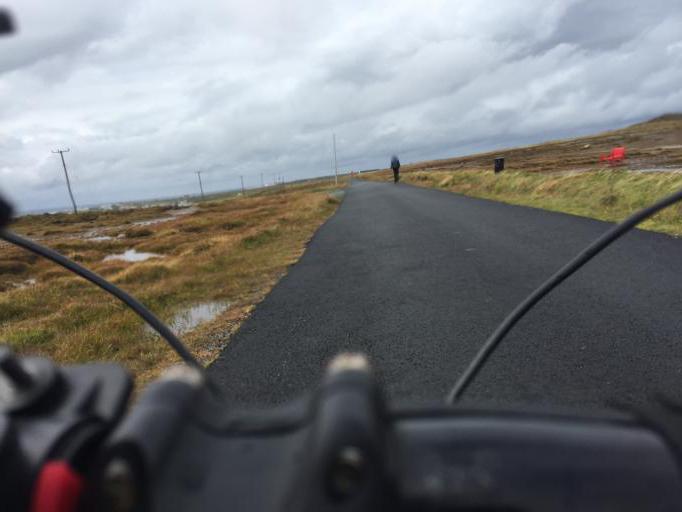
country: IE
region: Ulster
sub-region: County Donegal
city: Derrybeg
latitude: 55.2613
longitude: -8.2134
